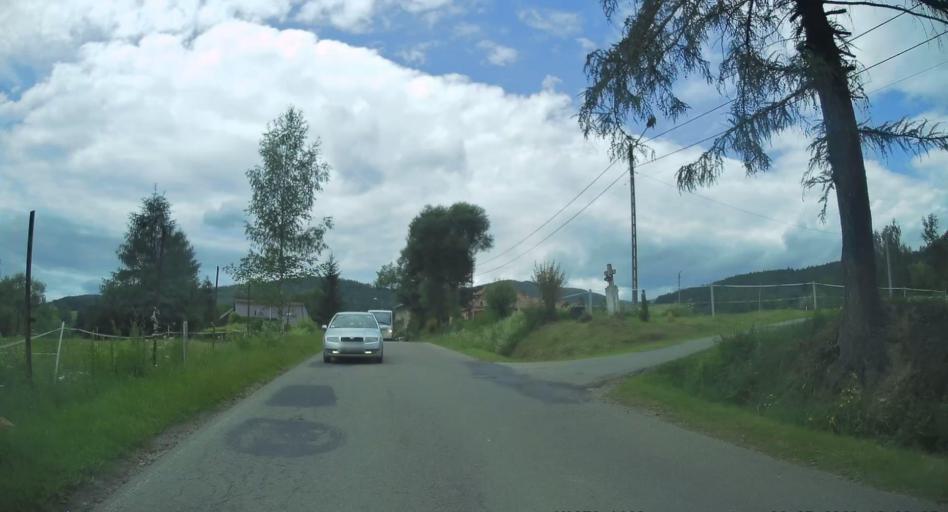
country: PL
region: Lesser Poland Voivodeship
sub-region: Powiat nowosadecki
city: Muszyna
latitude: 49.3859
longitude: 20.9152
